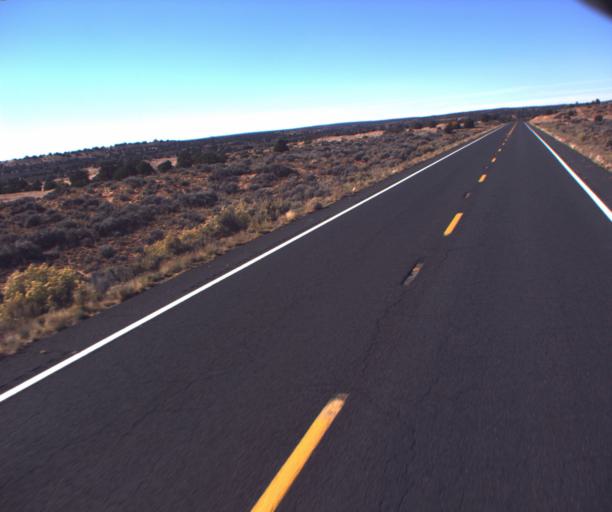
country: US
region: Arizona
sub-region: Coconino County
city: Kaibito
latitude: 36.5693
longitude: -110.7627
